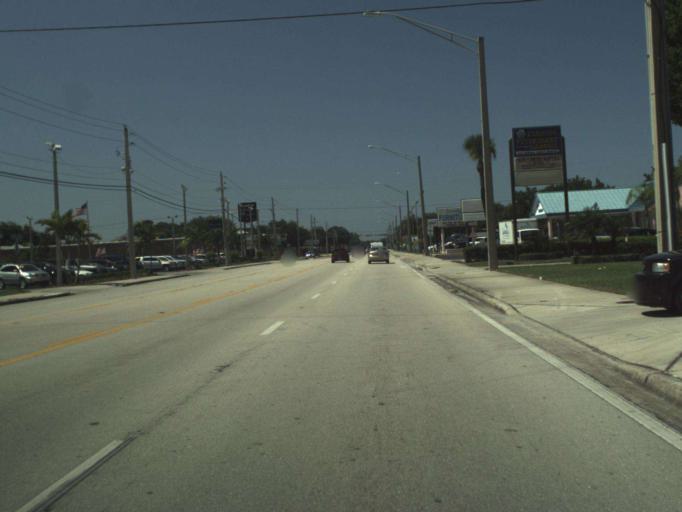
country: US
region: Florida
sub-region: Indian River County
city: Vero Beach
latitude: 27.6259
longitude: -80.3892
